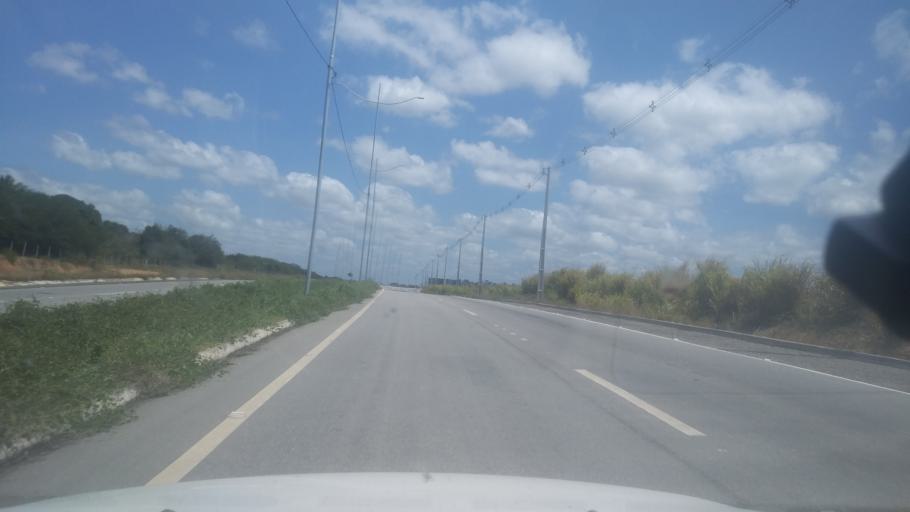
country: BR
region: Rio Grande do Norte
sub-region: Macaiba
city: Macaiba
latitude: -5.8377
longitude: -35.3748
